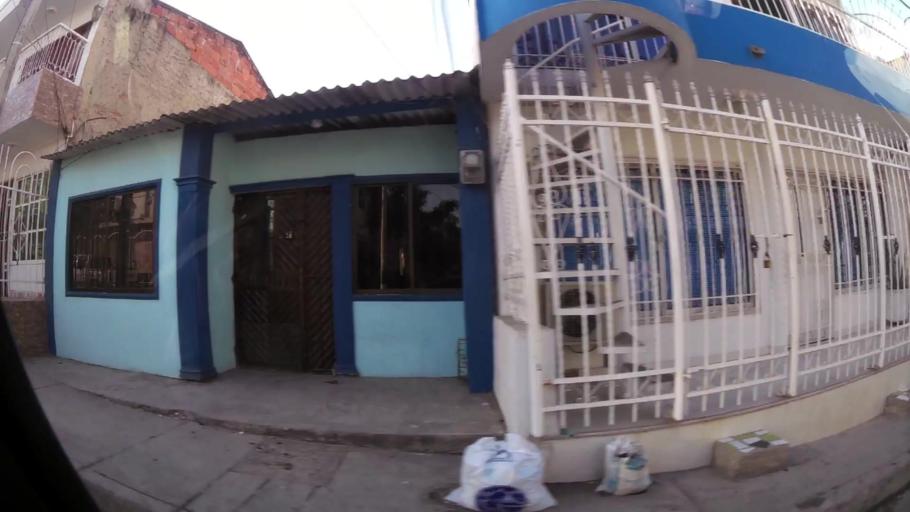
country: CO
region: Bolivar
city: Cartagena
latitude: 10.3979
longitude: -75.4777
